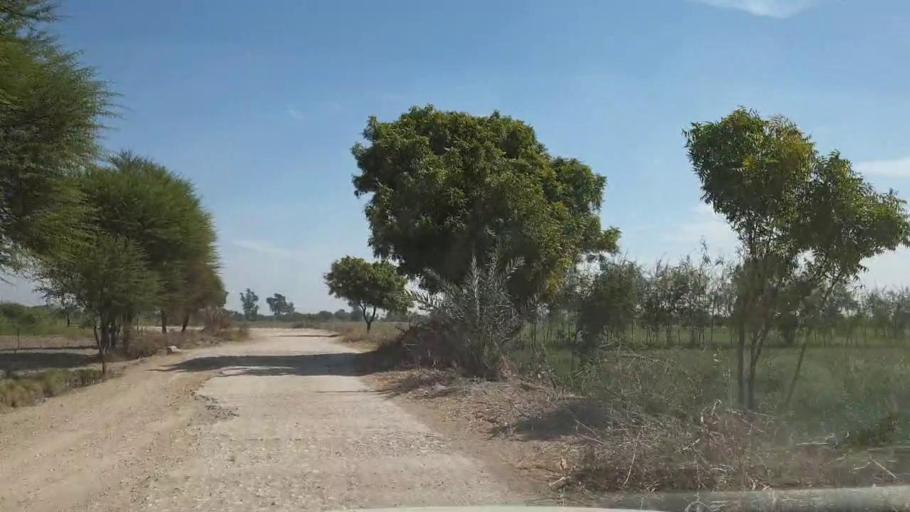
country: PK
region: Sindh
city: Pithoro
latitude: 25.6052
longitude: 69.2085
